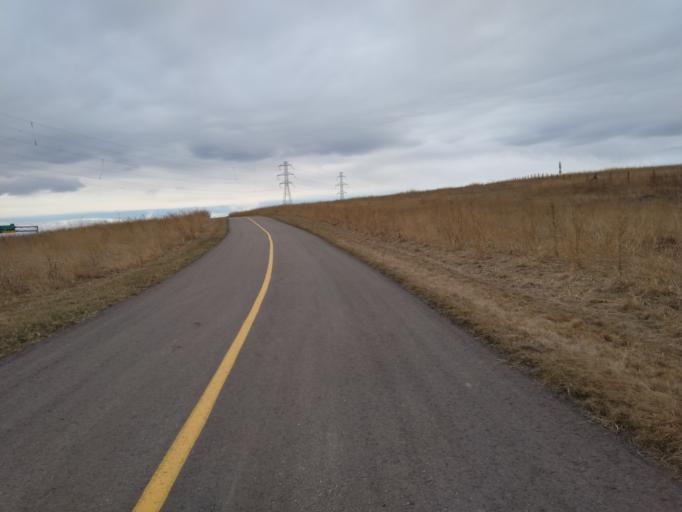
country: CA
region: Alberta
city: Airdrie
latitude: 51.1754
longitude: -114.0569
